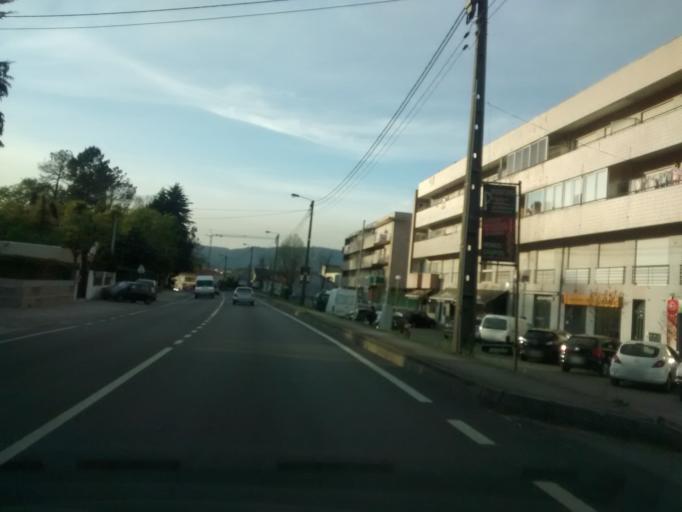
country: PT
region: Braga
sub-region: Guimaraes
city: Ponte
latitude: 41.4790
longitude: -8.3387
